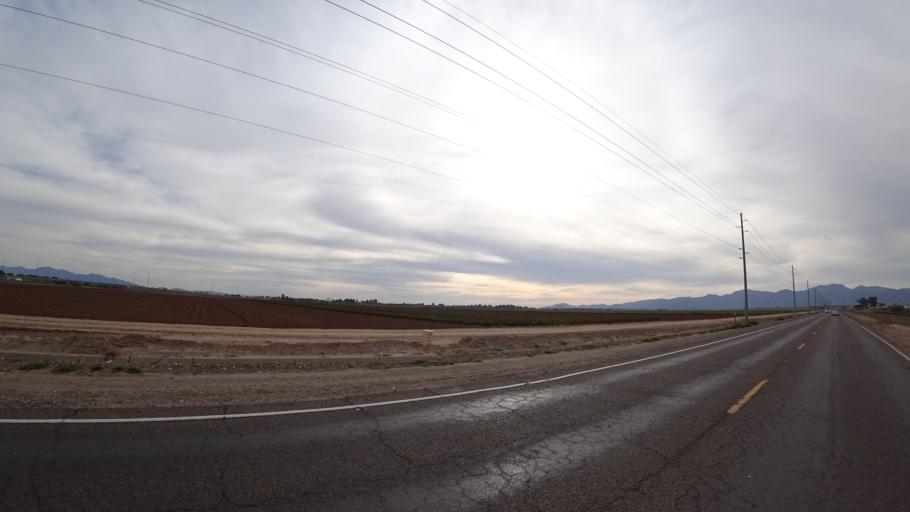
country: US
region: Arizona
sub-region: Maricopa County
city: Citrus Park
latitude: 33.5661
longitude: -112.3955
